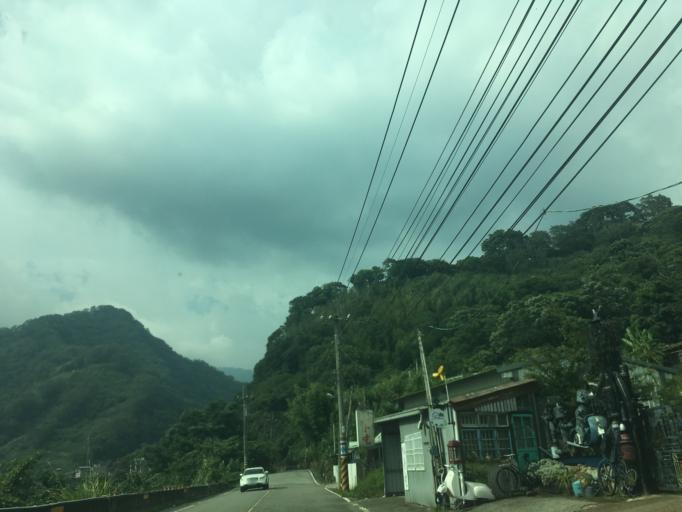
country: TW
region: Taiwan
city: Fengyuan
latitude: 24.3404
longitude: 120.9356
